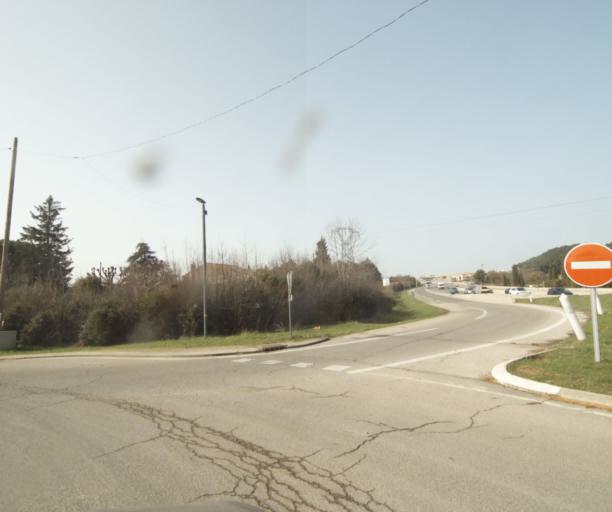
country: FR
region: Provence-Alpes-Cote d'Azur
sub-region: Departement des Bouches-du-Rhone
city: Meyreuil
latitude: 43.4734
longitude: 5.5151
